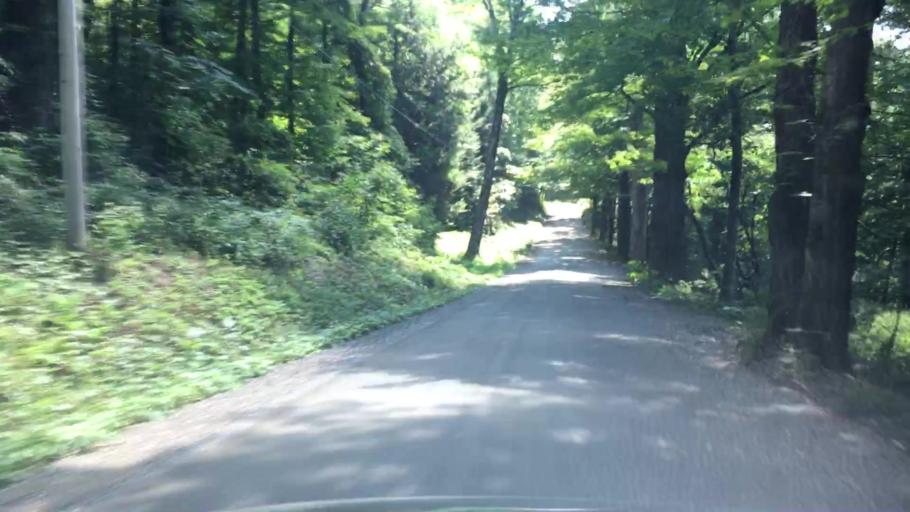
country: US
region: Vermont
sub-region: Windham County
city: West Brattleboro
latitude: 42.7973
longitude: -72.6358
